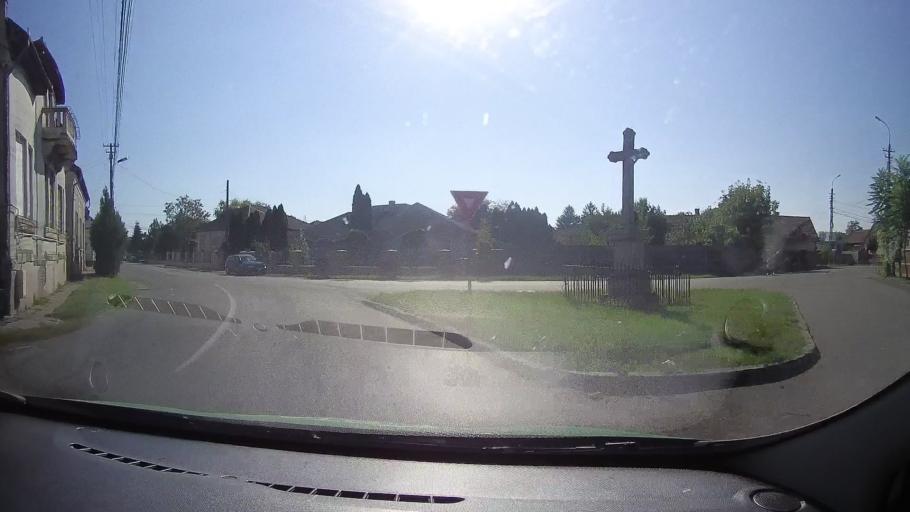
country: RO
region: Satu Mare
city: Carei
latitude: 47.6890
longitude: 22.4713
